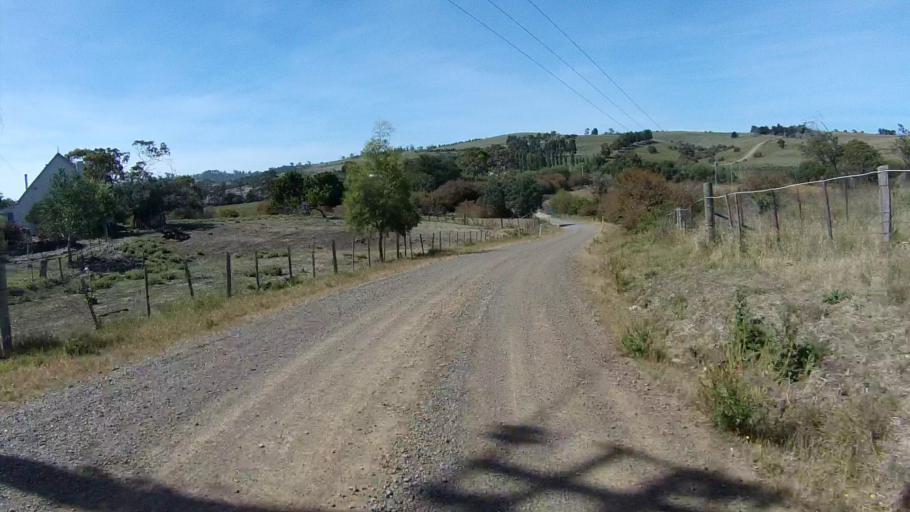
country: AU
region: Tasmania
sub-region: Sorell
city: Sorell
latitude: -42.7502
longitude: 147.6246
